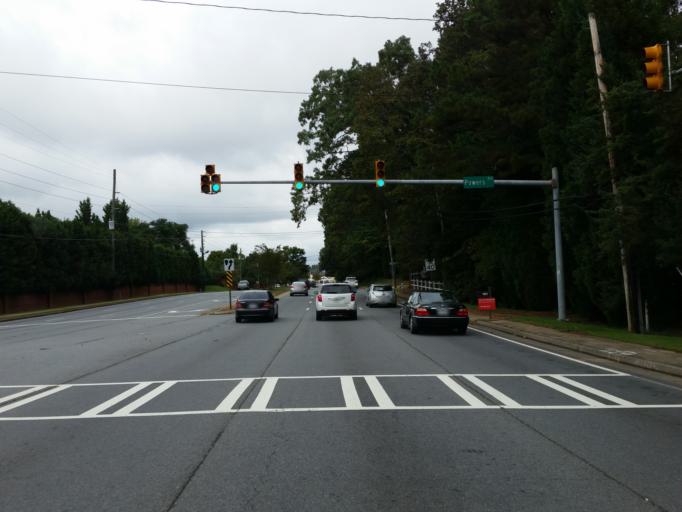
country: US
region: Georgia
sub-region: Fulton County
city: Sandy Springs
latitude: 33.9558
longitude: -84.4117
